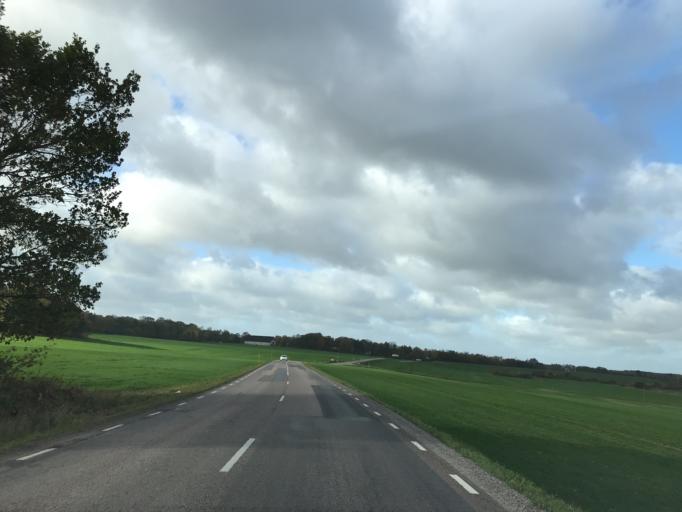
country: SE
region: Skane
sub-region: Svalovs Kommun
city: Kagerod
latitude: 56.0161
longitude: 13.0600
